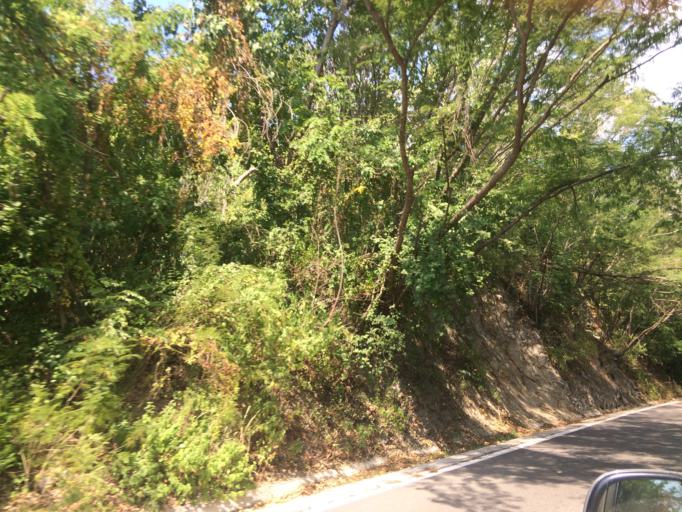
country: MX
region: Jalisco
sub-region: Cihuatlan
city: Emiliano Zapata (El Ranchito)
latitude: 19.2474
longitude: -104.7178
